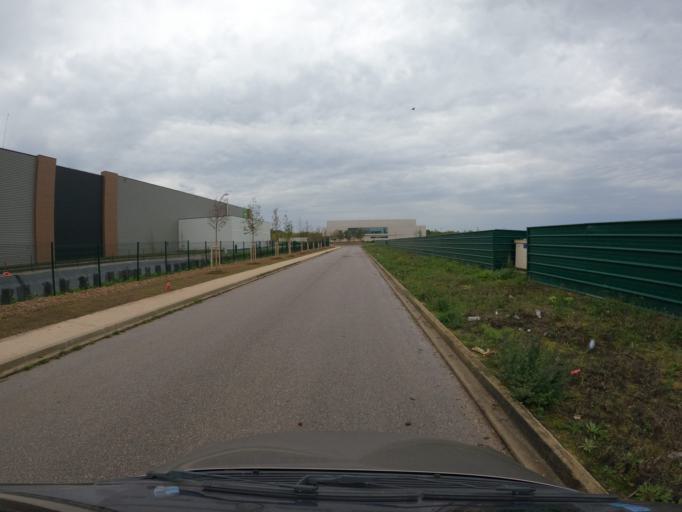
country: FR
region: Ile-de-France
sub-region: Departement de Seine-et-Marne
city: Serris
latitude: 48.8381
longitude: 2.8003
